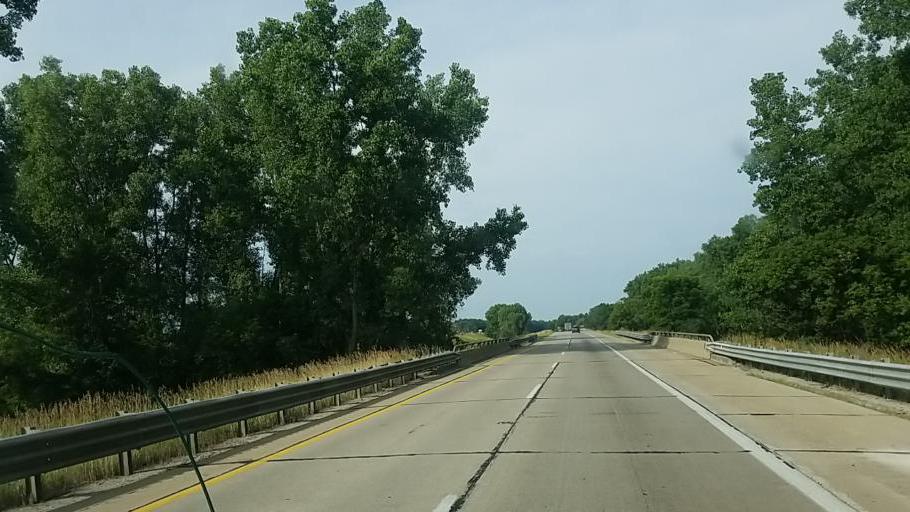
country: US
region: Michigan
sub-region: Eaton County
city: Olivet
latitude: 42.4732
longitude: -84.8912
